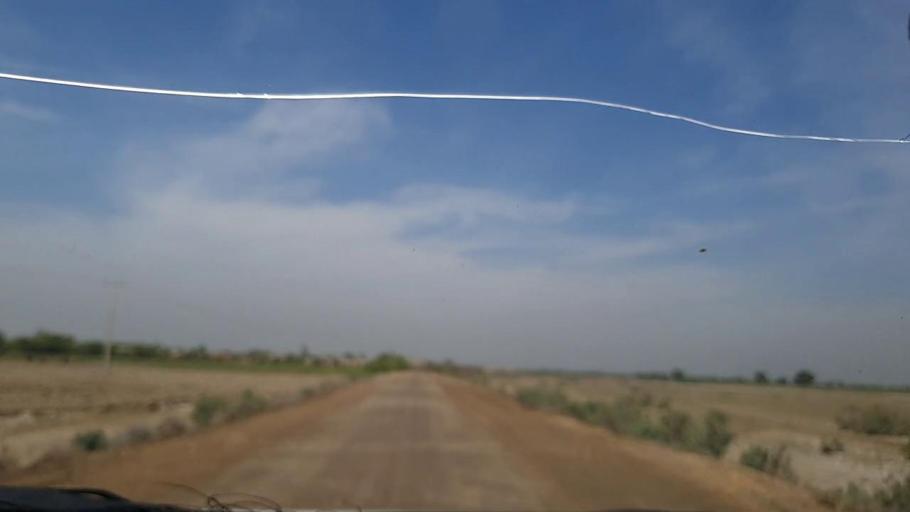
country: PK
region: Sindh
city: Pithoro
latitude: 25.4925
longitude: 69.4564
